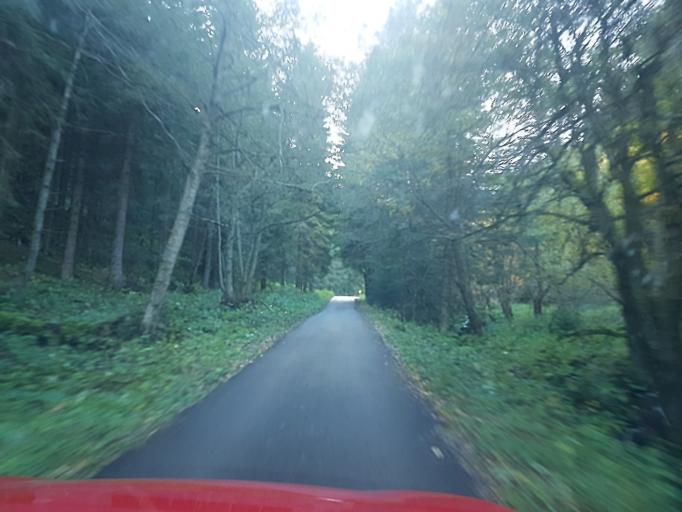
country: SK
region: Zilinsky
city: Ruzomberok
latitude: 48.9980
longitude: 19.2407
